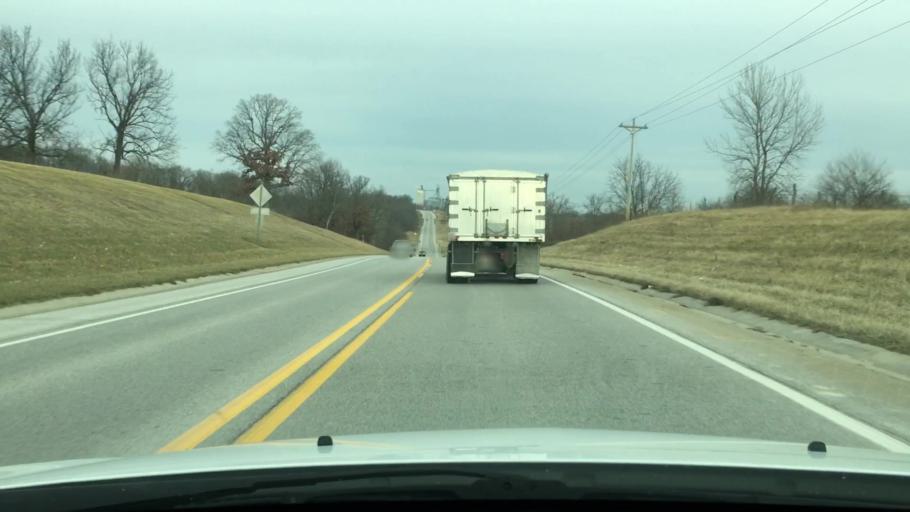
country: US
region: Illinois
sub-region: Pike County
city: Pittsfield
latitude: 39.6612
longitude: -90.7740
